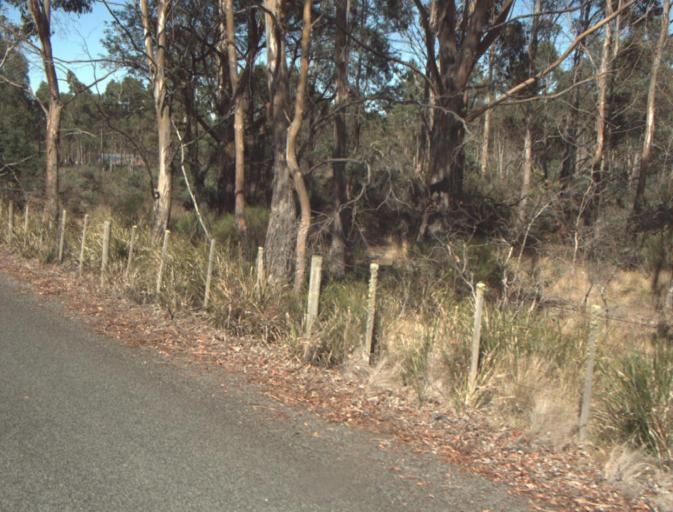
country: AU
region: Tasmania
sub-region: Launceston
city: Newstead
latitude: -41.3715
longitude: 147.2981
